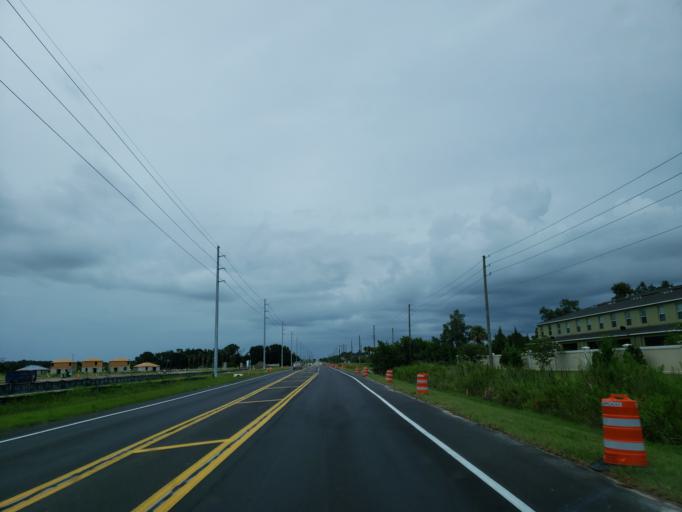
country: US
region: Florida
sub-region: Hillsborough County
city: Ruskin
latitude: 27.7349
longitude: -82.4053
